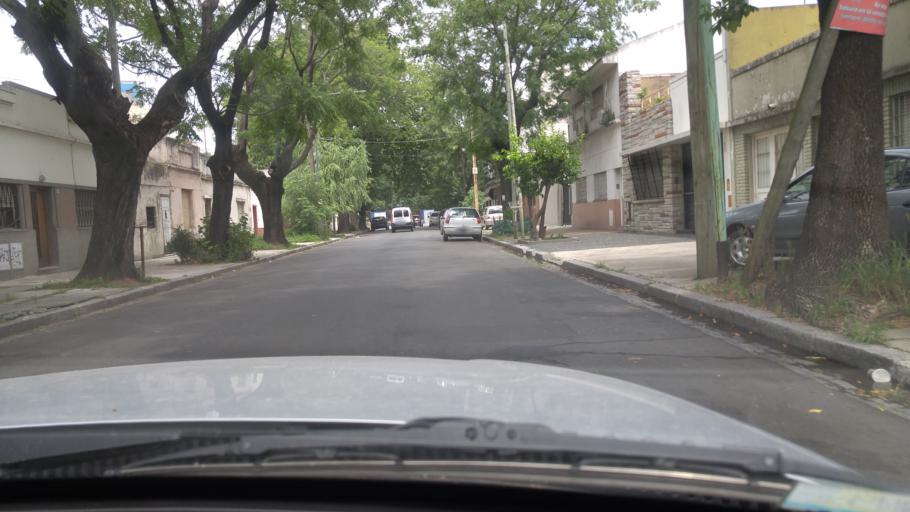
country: AR
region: Buenos Aires F.D.
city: Villa Santa Rita
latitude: -34.6323
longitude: -58.5145
